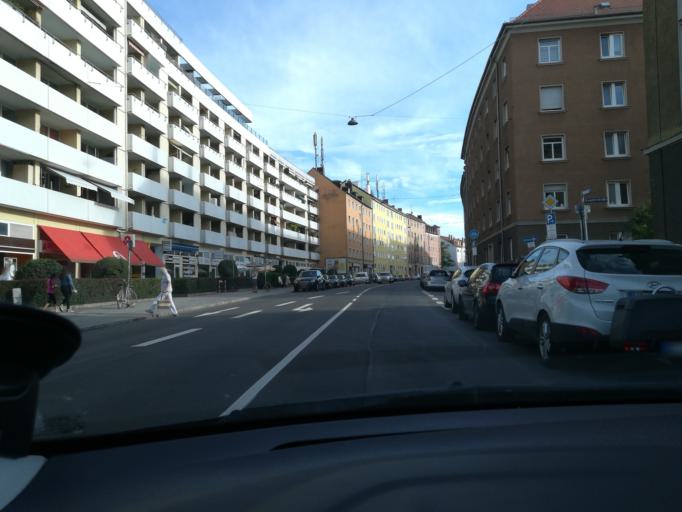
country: DE
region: Bavaria
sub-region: Upper Bavaria
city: Munich
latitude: 48.1249
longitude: 11.5410
